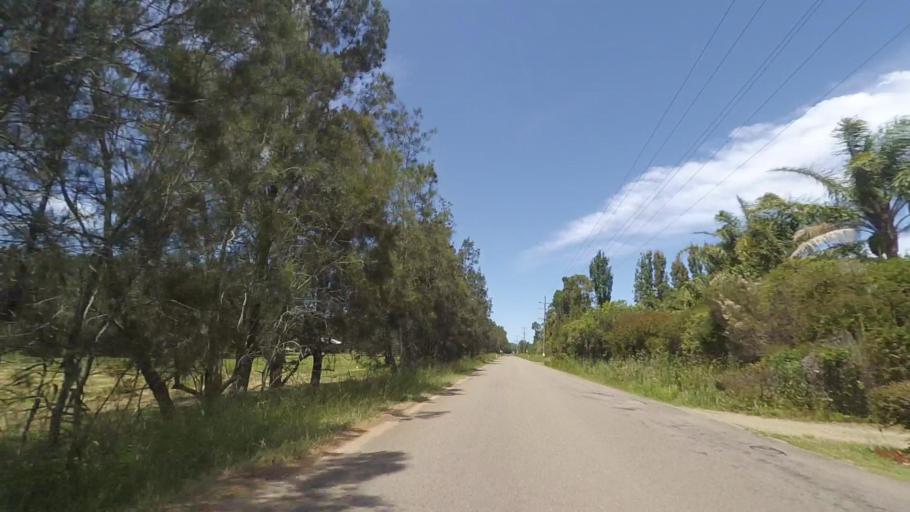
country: AU
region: New South Wales
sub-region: Port Stephens Shire
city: Port Stephens
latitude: -32.7671
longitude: 152.0043
